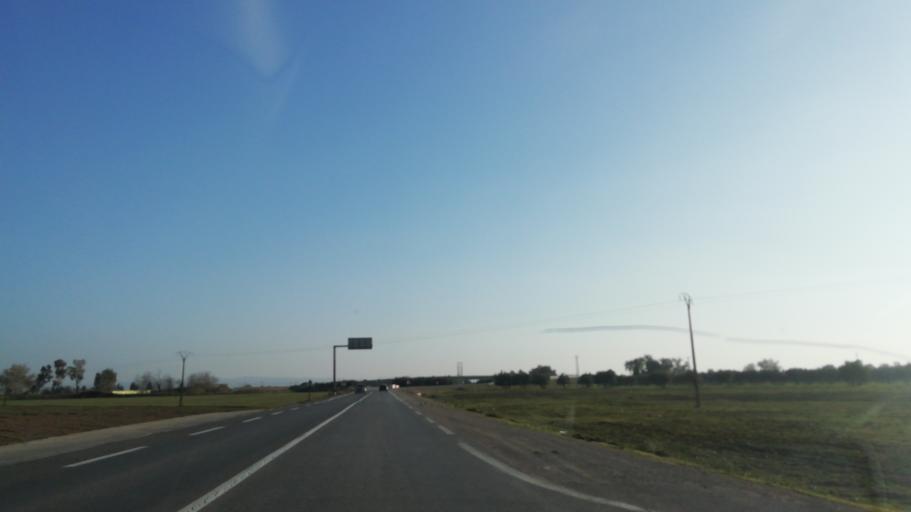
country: DZ
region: Sidi Bel Abbes
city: Sidi Bel Abbes
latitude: 35.1767
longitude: -0.6860
